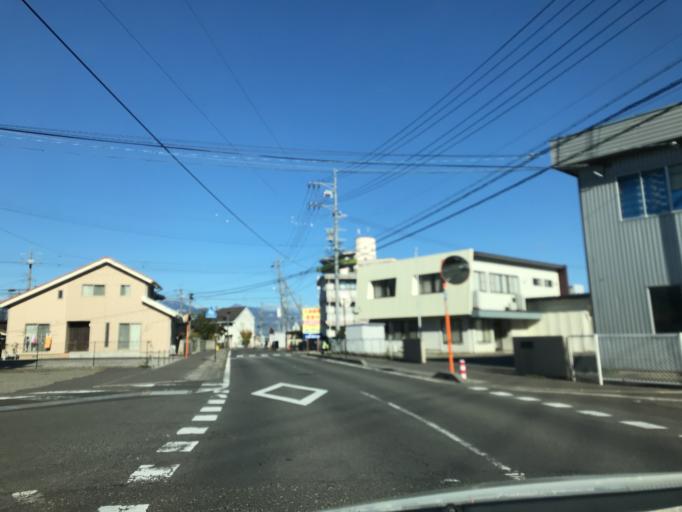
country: JP
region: Nagano
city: Shiojiri
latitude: 36.1172
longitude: 137.9471
